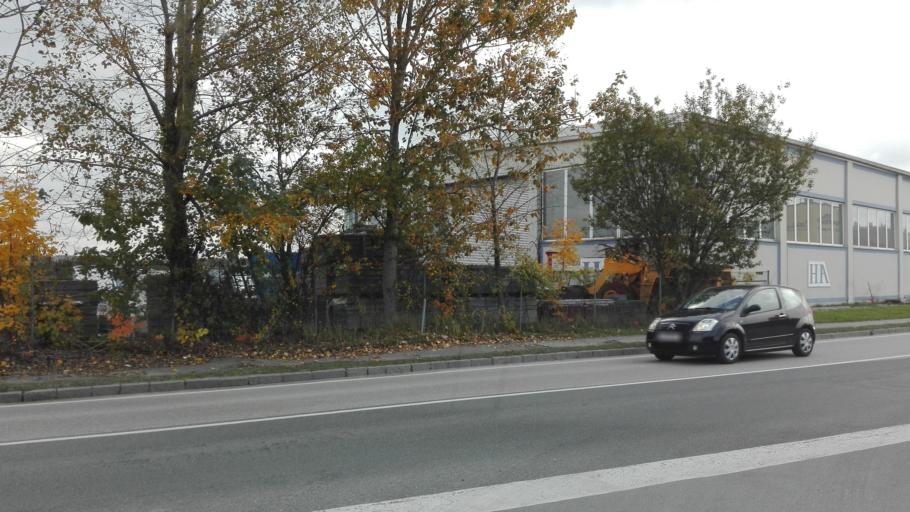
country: AT
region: Upper Austria
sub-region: Politischer Bezirk Urfahr-Umgebung
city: Feldkirchen an der Donau
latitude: 48.3622
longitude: 14.0063
